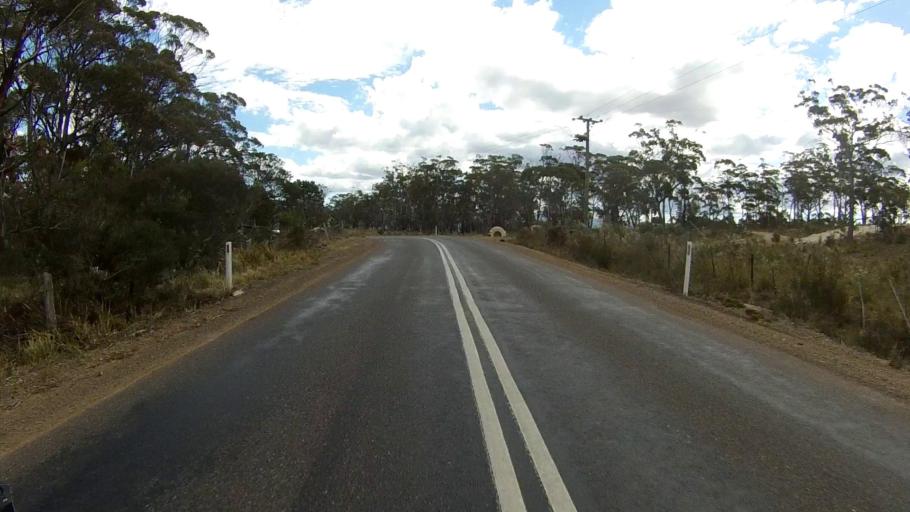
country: AU
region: Tasmania
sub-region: Break O'Day
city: St Helens
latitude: -41.9865
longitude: 148.1287
